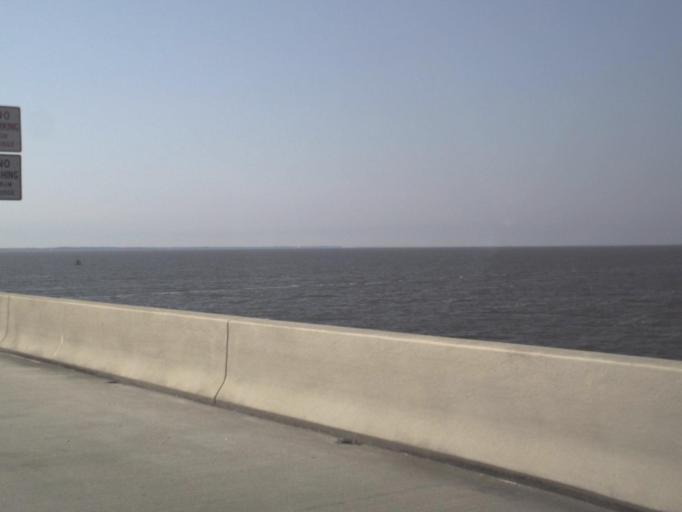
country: US
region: Florida
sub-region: Franklin County
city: Eastpoint
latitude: 29.7039
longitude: -84.8905
